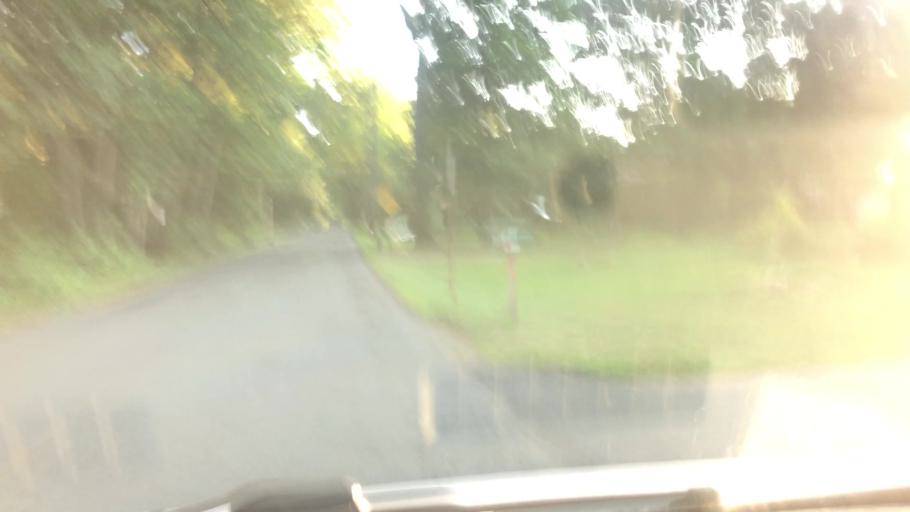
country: US
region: Massachusetts
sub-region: Hampshire County
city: Easthampton
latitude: 42.2928
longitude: -72.7166
